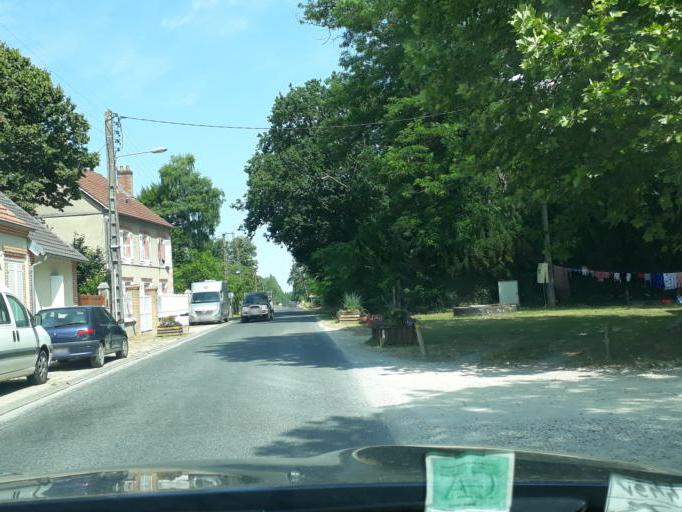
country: FR
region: Centre
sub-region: Departement du Loir-et-Cher
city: Vouzon
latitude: 47.6489
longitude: 2.0565
